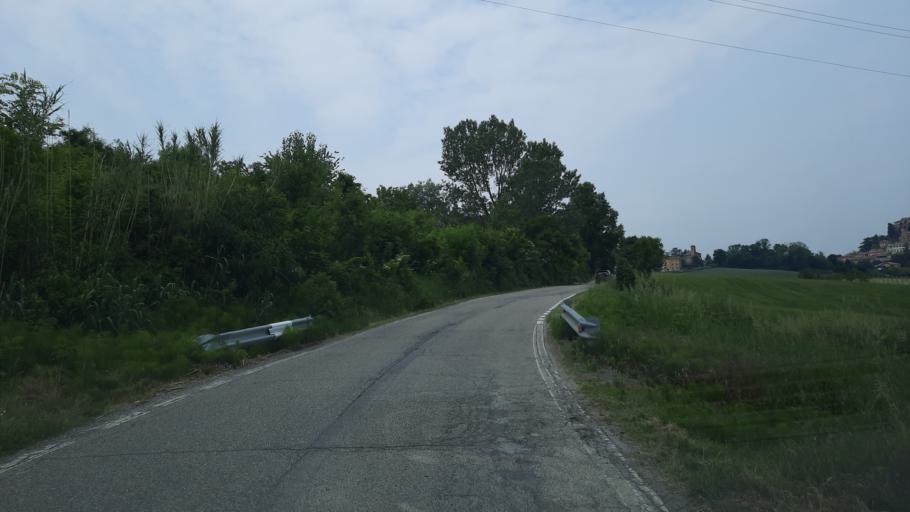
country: IT
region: Piedmont
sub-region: Provincia di Alessandria
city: Ozzano Monferrato
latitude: 45.0971
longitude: 8.3838
